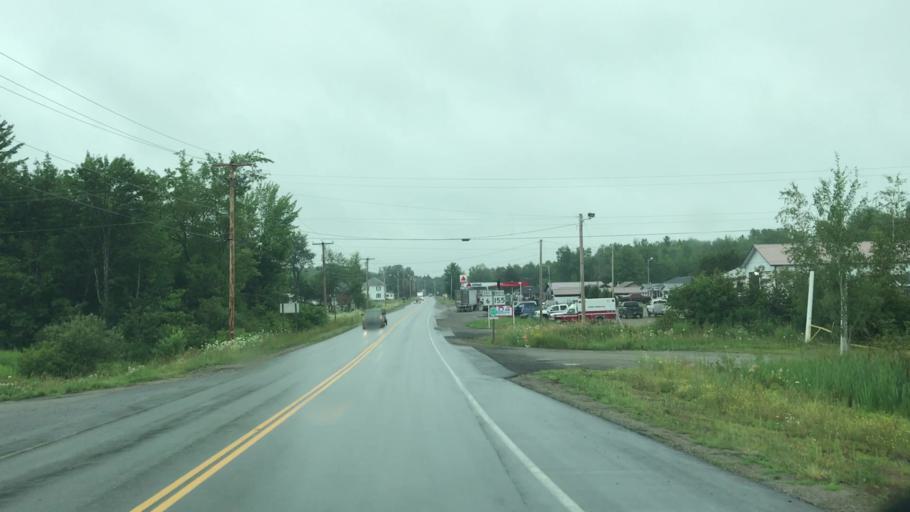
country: US
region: Maine
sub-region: Penobscot County
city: Howland
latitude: 45.2367
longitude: -68.6741
